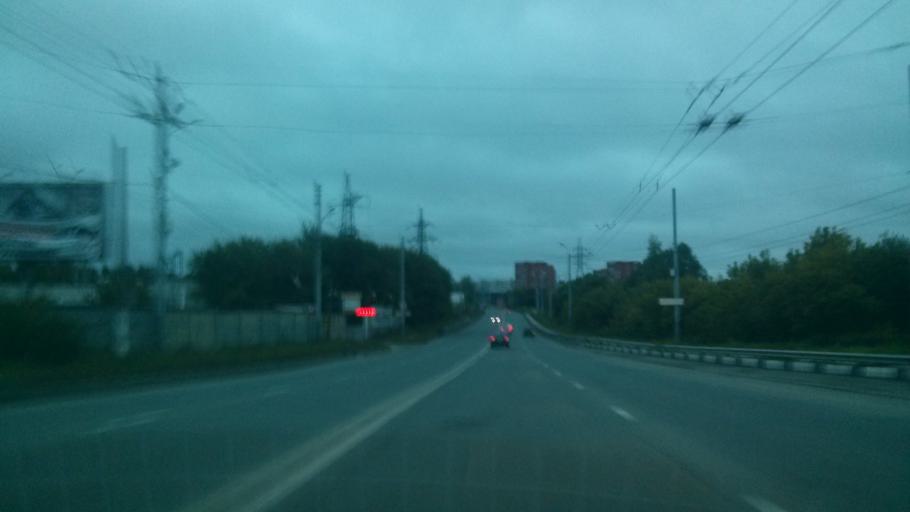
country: RU
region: Nizjnij Novgorod
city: Afonino
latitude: 56.3012
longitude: 44.0555
